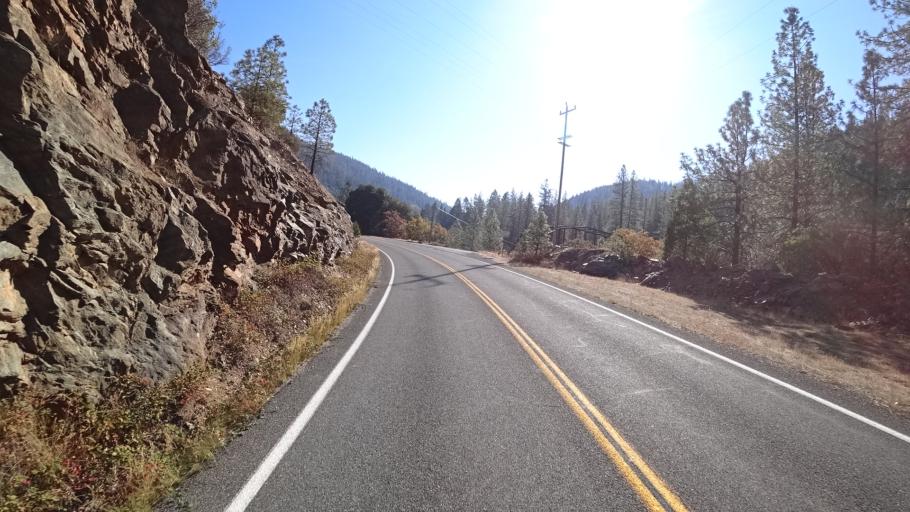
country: US
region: California
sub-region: Siskiyou County
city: Happy Camp
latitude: 41.7758
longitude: -123.0354
